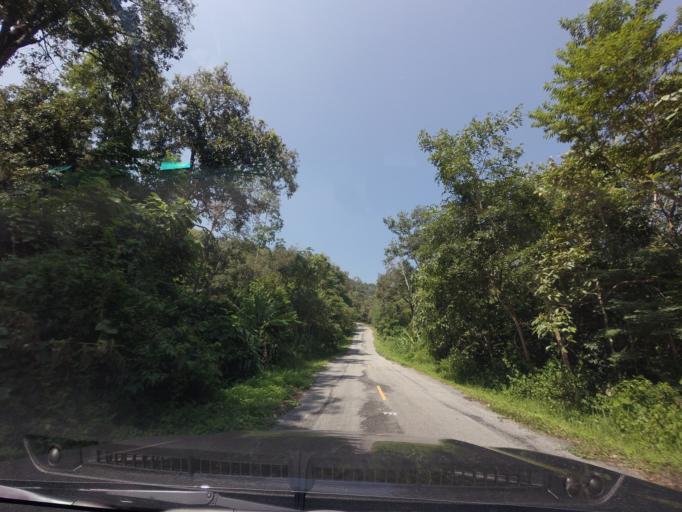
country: TH
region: Loei
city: Na Haeo
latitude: 17.5680
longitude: 100.9723
